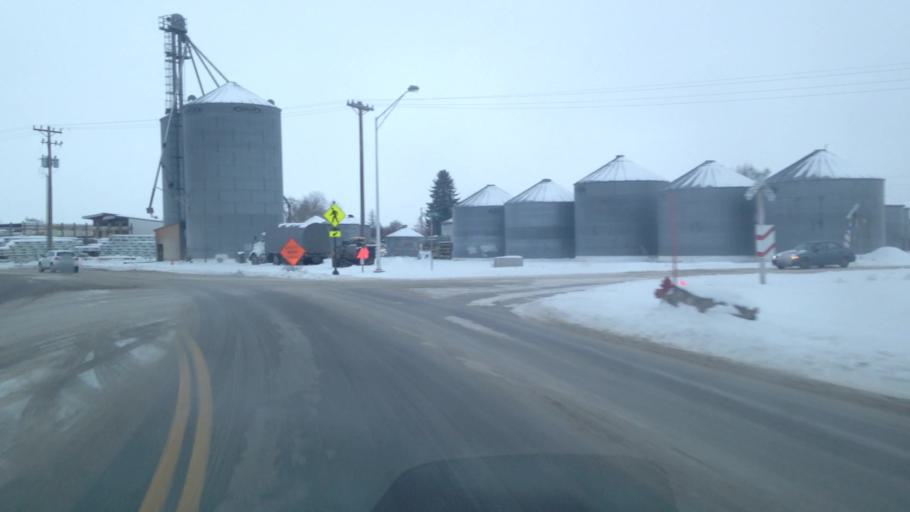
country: US
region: Idaho
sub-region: Madison County
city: Rexburg
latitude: 43.8281
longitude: -111.7889
